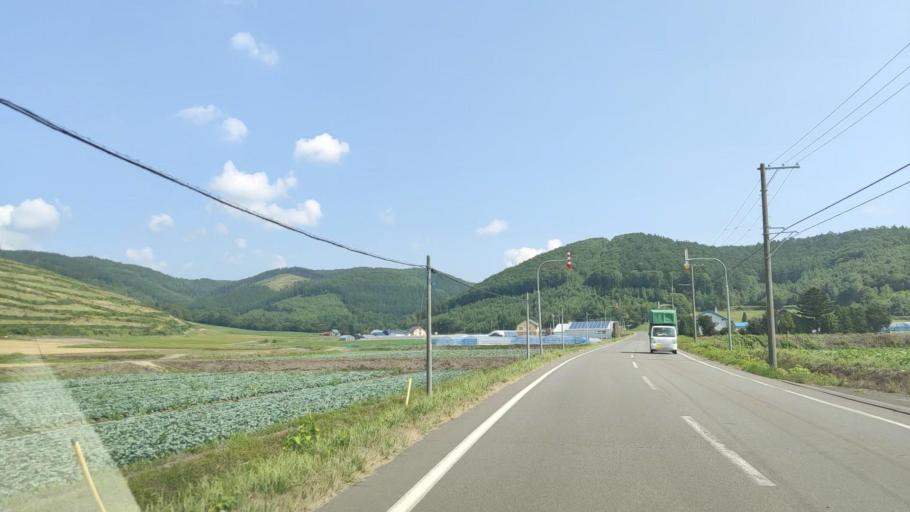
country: JP
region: Hokkaido
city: Shimo-furano
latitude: 43.4161
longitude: 142.3999
